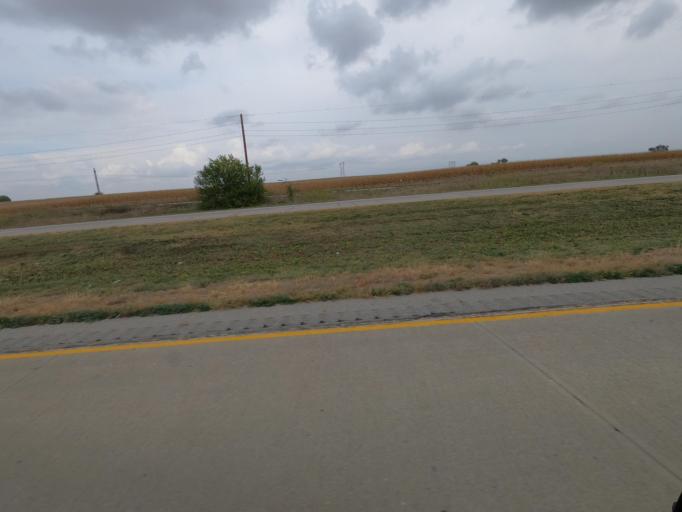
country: US
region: Iowa
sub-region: Jasper County
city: Prairie City
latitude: 41.5710
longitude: -93.1671
